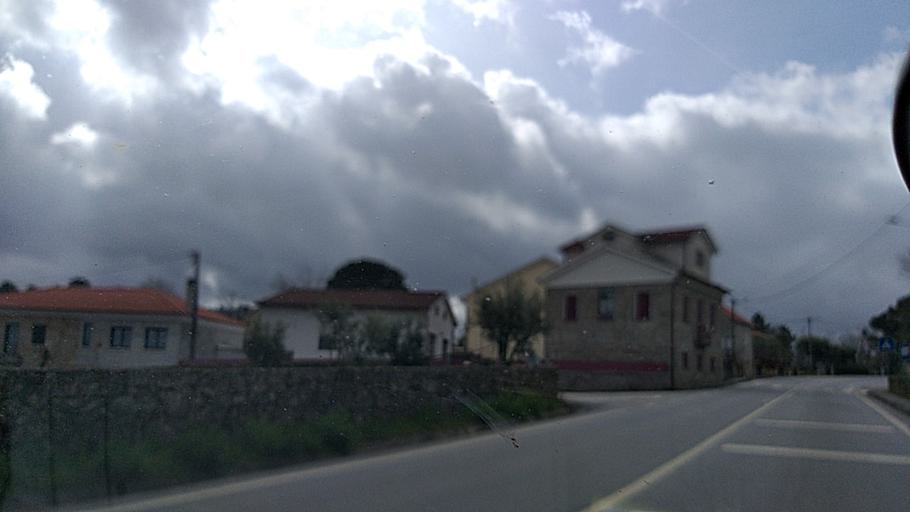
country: PT
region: Viseu
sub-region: Mangualde
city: Mangualde
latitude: 40.6295
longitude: -7.7487
